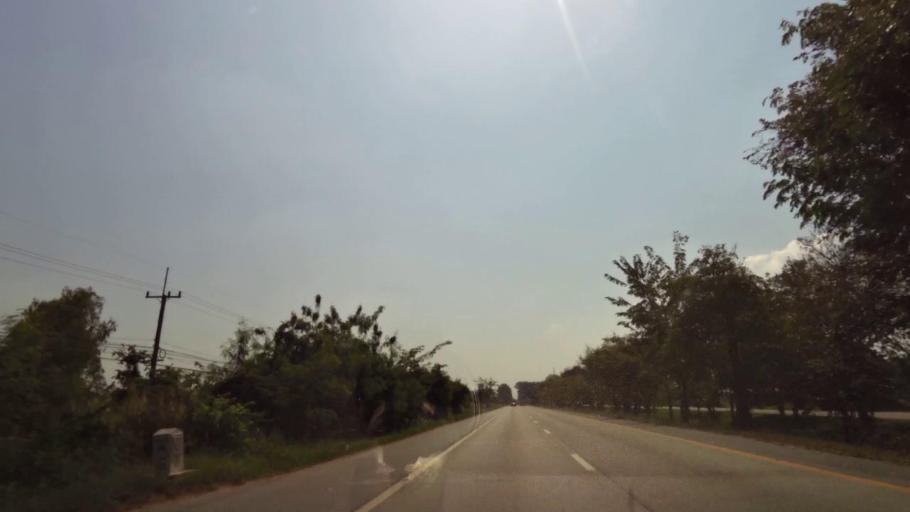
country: TH
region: Phichit
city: Wachira Barami
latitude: 16.5843
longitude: 100.1474
